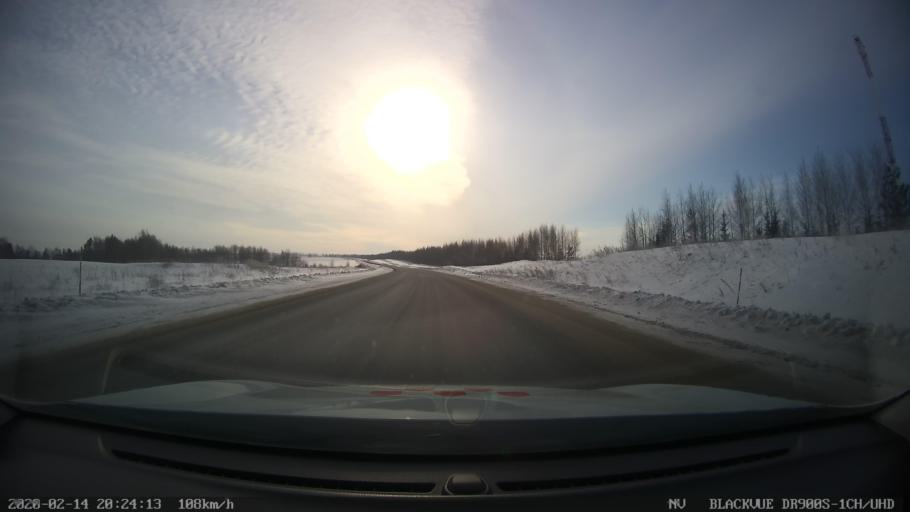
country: RU
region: Tatarstan
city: Verkhniy Uslon
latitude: 55.5158
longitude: 48.9672
